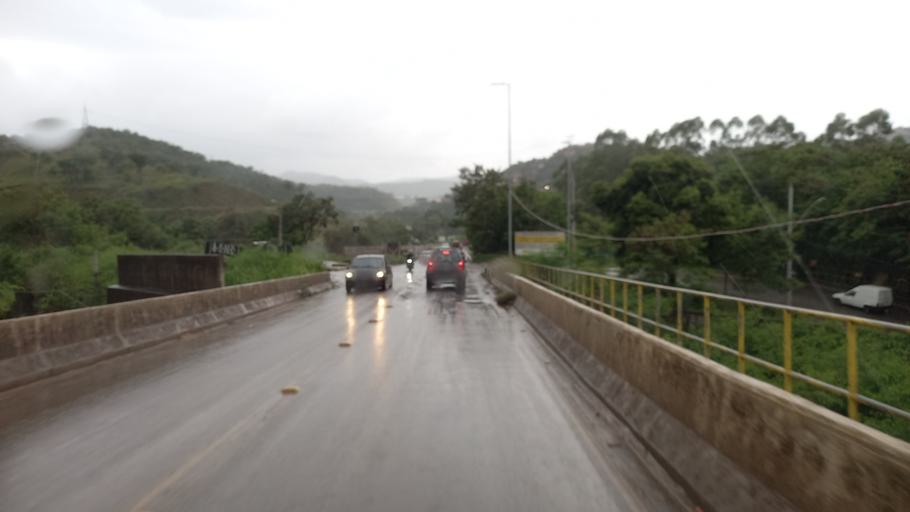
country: BR
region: Minas Gerais
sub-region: Belo Horizonte
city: Belo Horizonte
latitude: -19.8767
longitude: -43.8600
